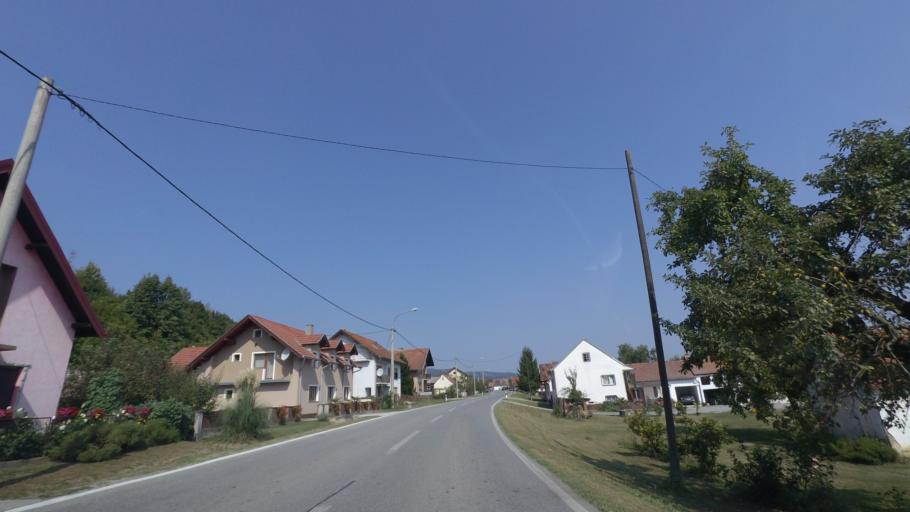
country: HR
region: Brodsko-Posavska
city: Resetari
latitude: 45.3718
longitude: 17.5190
